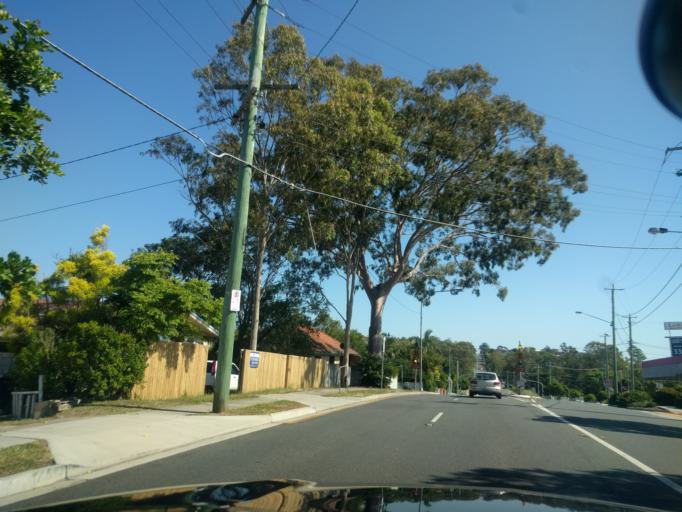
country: AU
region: Queensland
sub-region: Brisbane
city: Chermside West
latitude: -27.3847
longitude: 153.0125
